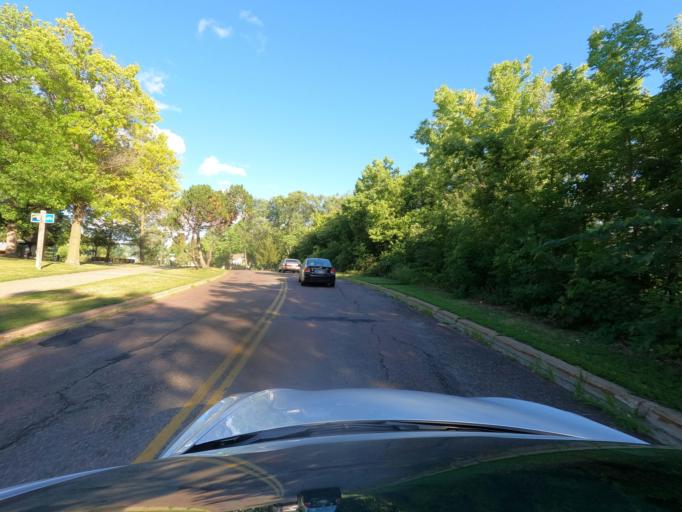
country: US
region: Minnesota
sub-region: Hennepin County
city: Saint Anthony
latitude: 45.0241
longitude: -93.2433
